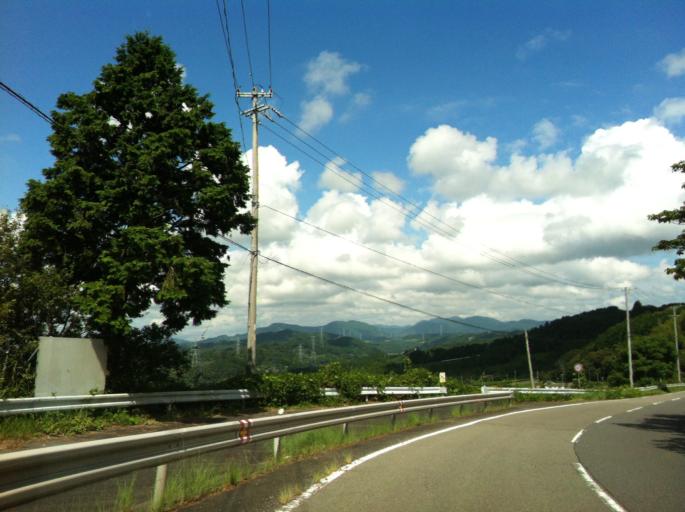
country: JP
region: Shizuoka
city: Kanaya
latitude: 34.7799
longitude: 138.1388
